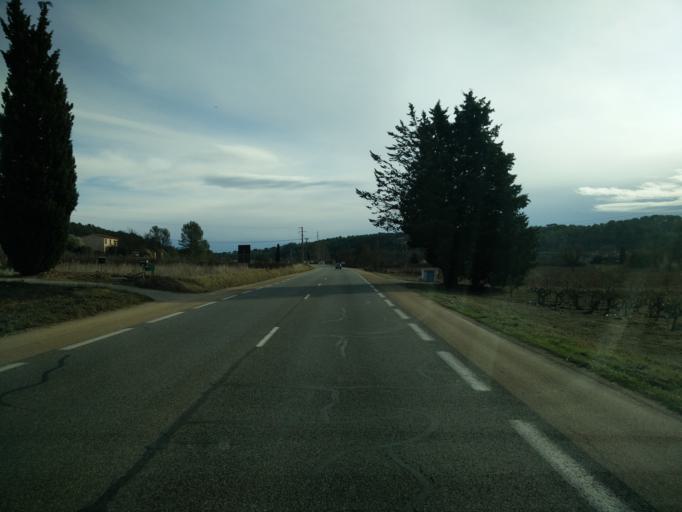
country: FR
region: Provence-Alpes-Cote d'Azur
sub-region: Departement du Var
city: Lorgues
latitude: 43.4805
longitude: 6.3712
